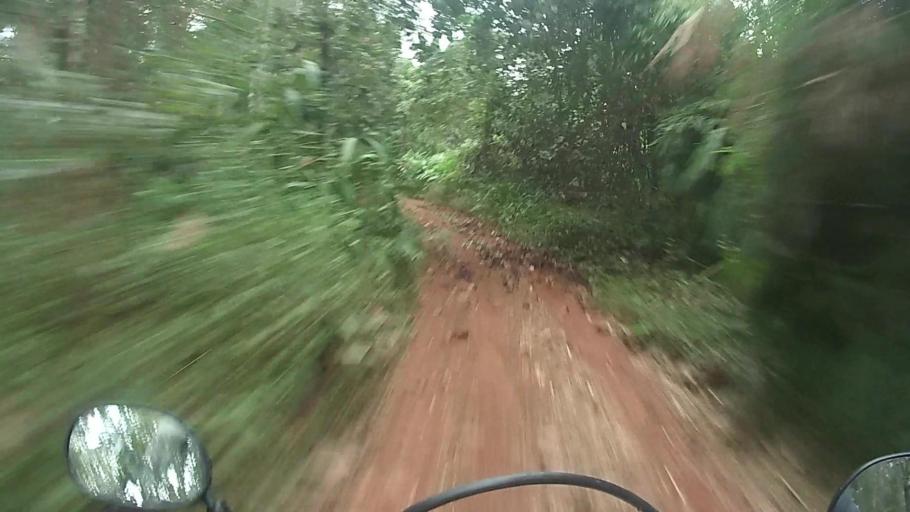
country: TH
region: Chiang Mai
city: Mae On
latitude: 18.8924
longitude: 99.2159
